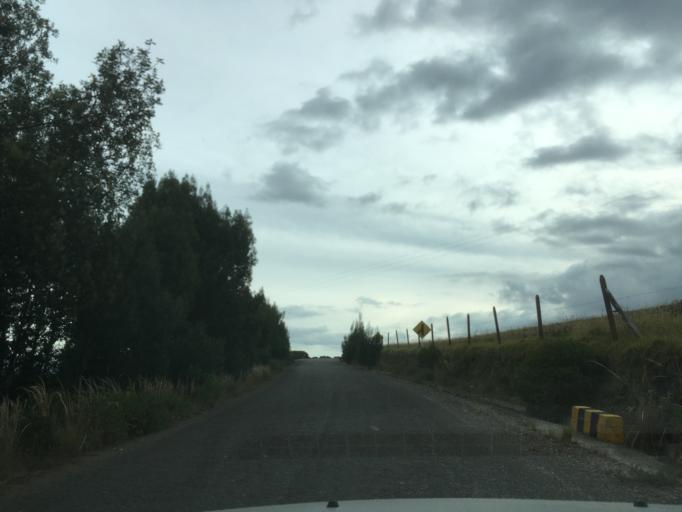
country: CO
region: Boyaca
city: Firavitoba
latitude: 5.6809
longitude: -73.0329
